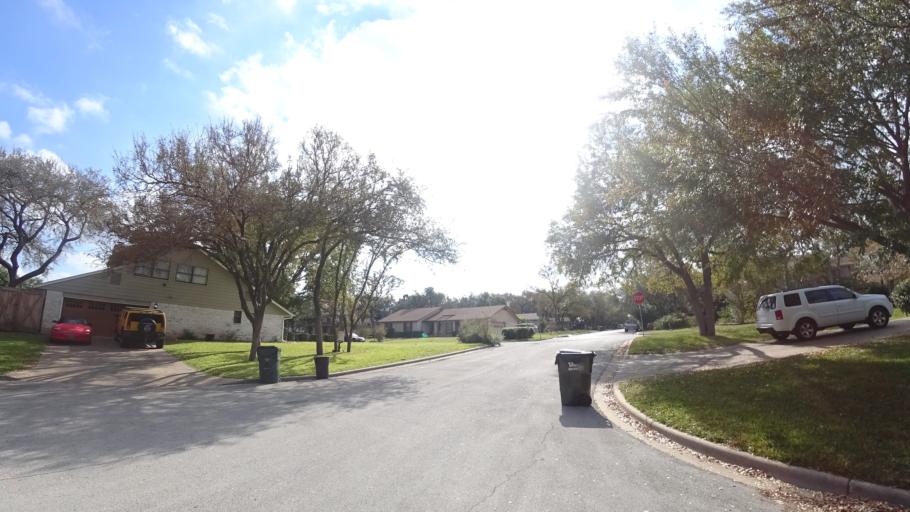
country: US
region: Texas
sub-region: Travis County
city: Shady Hollow
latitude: 30.1666
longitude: -97.8582
